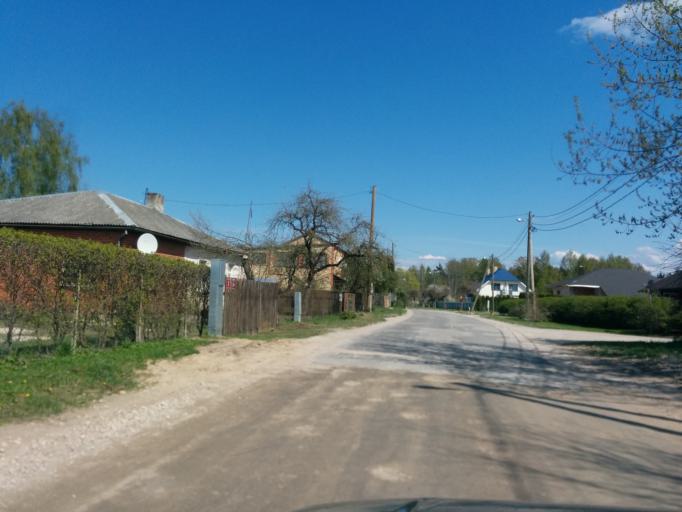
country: LV
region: Jelgava
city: Jelgava
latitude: 56.6282
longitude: 23.7315
